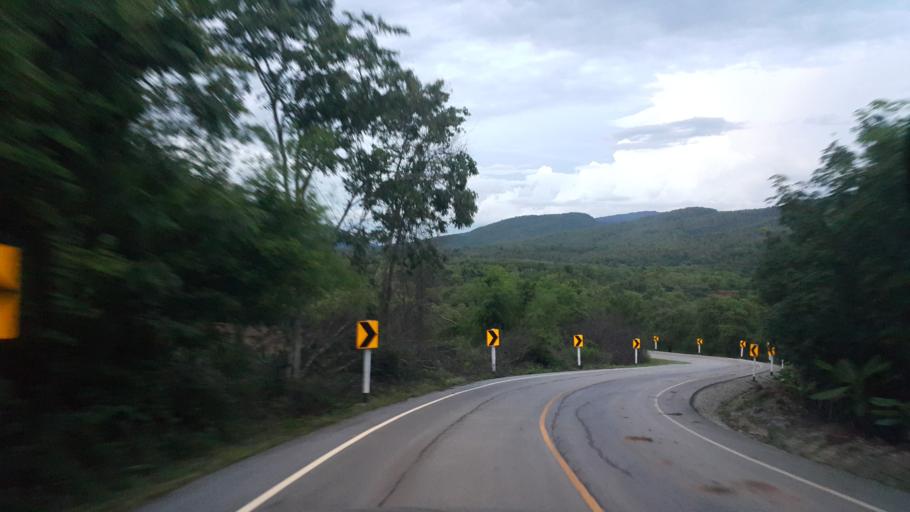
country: TH
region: Loei
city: Phu Ruea
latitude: 17.5154
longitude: 101.2322
